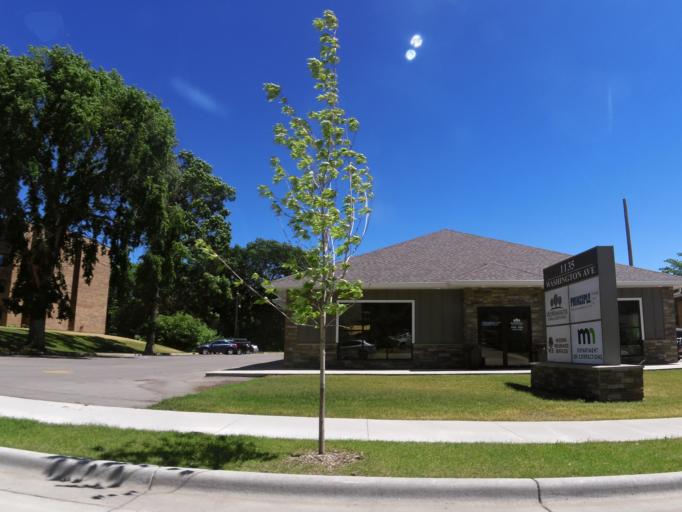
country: US
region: Minnesota
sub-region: Becker County
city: Detroit Lakes
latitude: 46.8125
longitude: -95.8456
